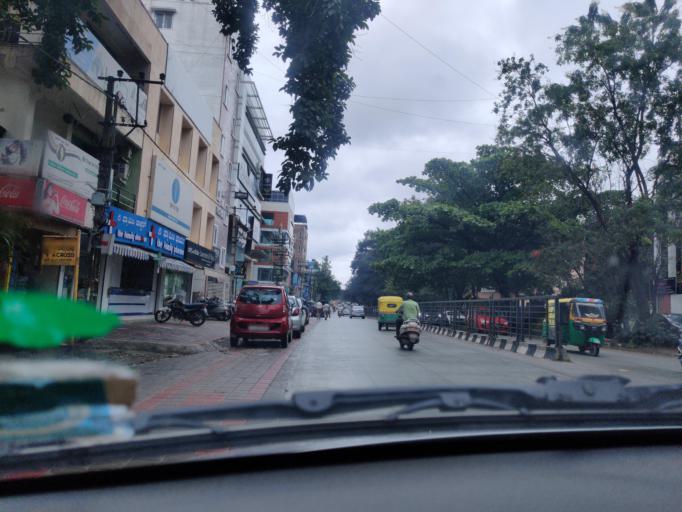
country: IN
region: Karnataka
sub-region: Bangalore Urban
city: Bangalore
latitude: 13.0204
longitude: 77.6434
